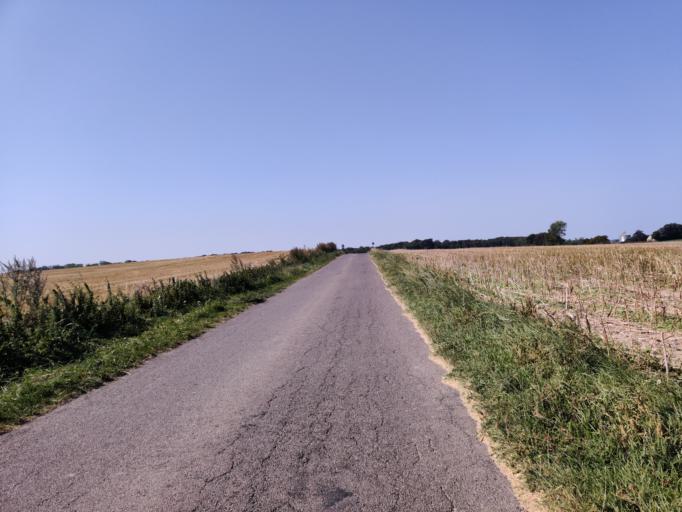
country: DK
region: Zealand
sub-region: Guldborgsund Kommune
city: Nykobing Falster
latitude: 54.6822
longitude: 11.8988
